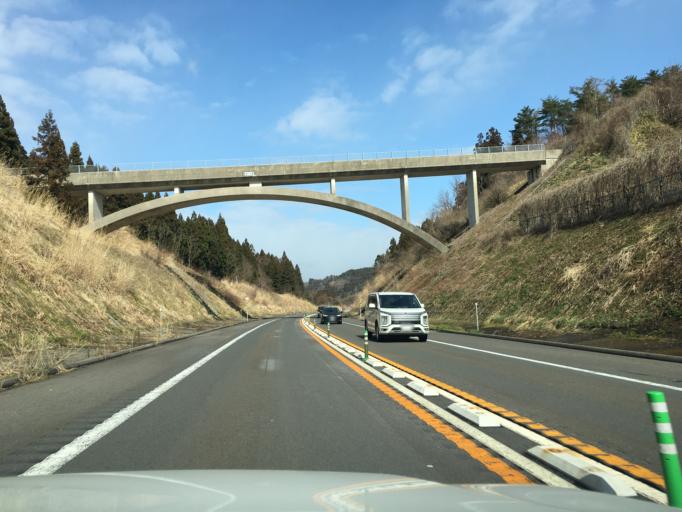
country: JP
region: Akita
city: Akita
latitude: 39.7676
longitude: 140.1224
